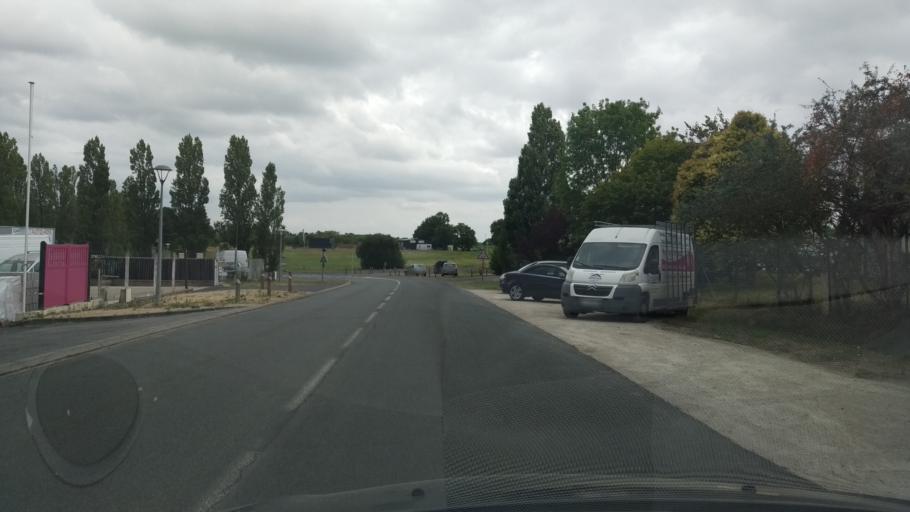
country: FR
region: Poitou-Charentes
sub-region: Departement de la Vienne
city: Smarves
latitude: 46.5059
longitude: 0.3603
